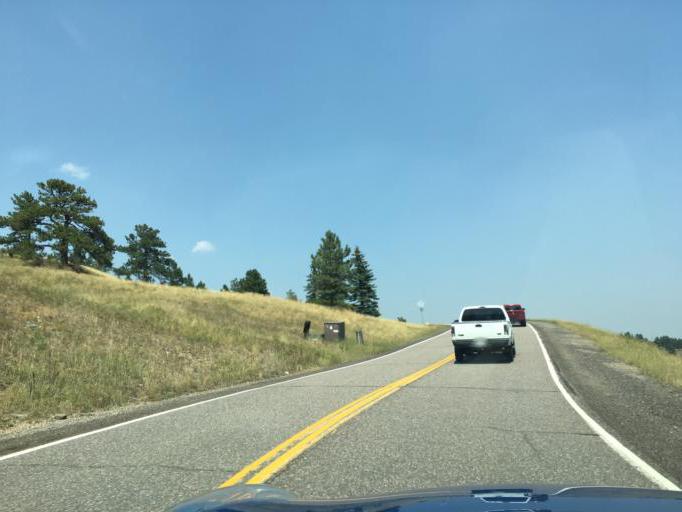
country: US
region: Colorado
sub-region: Jefferson County
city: Genesee
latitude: 39.7038
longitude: -105.2805
